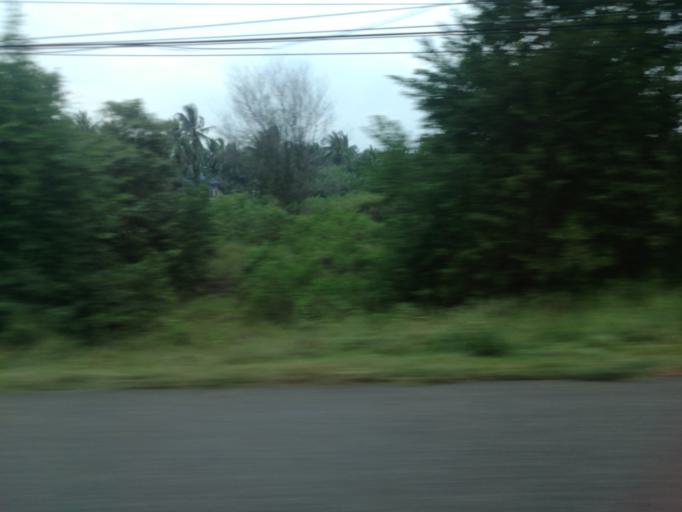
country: TH
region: Prachuap Khiri Khan
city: Kui Buri
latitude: 12.0302
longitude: 99.8431
